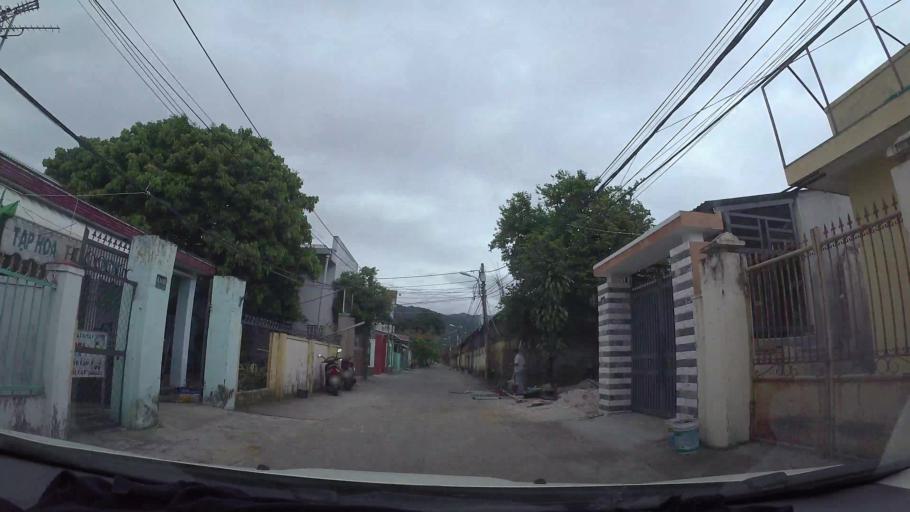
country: VN
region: Da Nang
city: Lien Chieu
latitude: 16.1217
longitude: 108.1164
